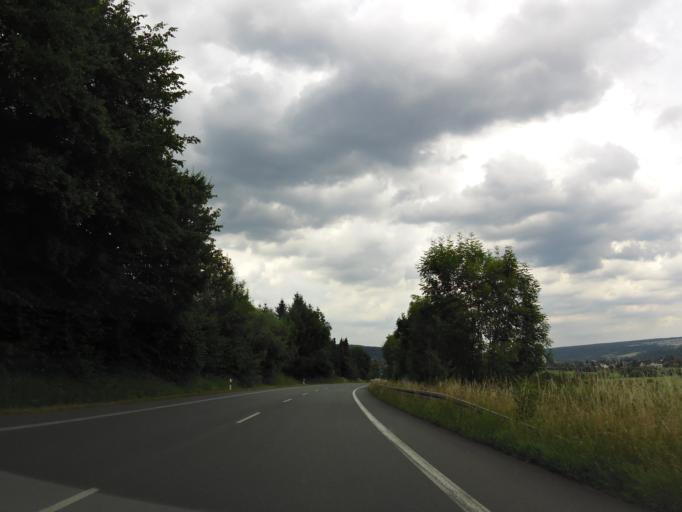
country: DE
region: North Rhine-Westphalia
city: Beverungen
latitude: 51.6508
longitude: 9.3708
